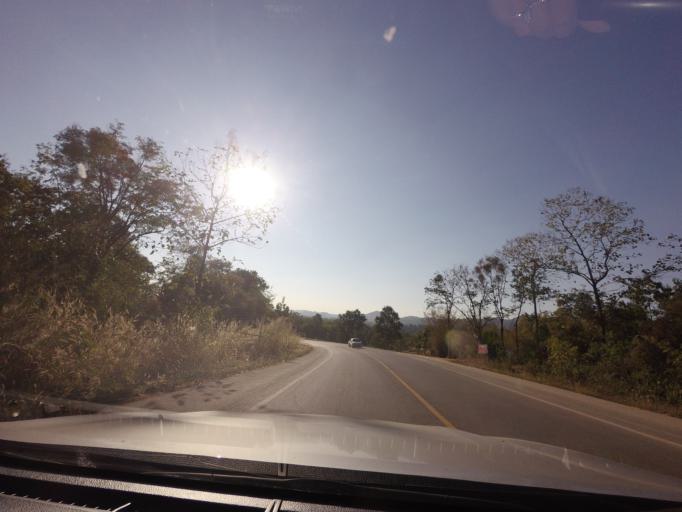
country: TH
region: Lampang
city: Mae Mo
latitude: 18.4843
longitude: 99.6372
